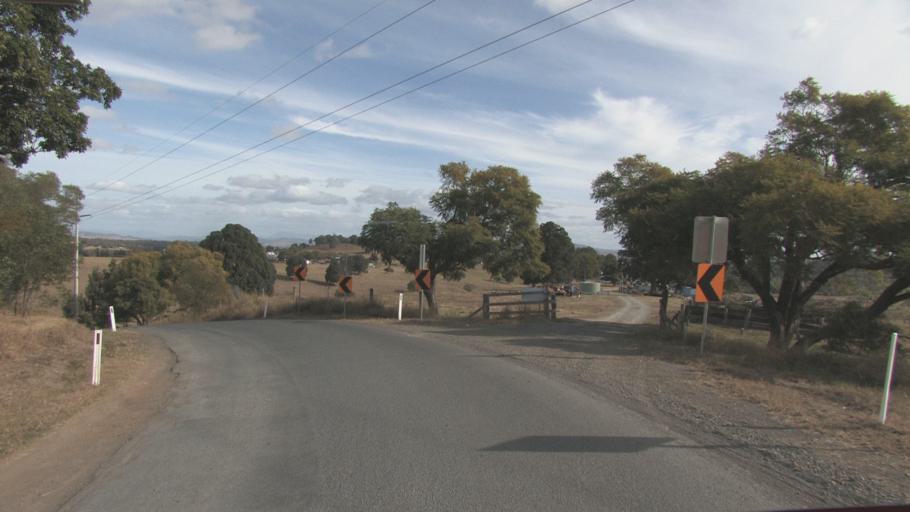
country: AU
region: Queensland
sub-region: Logan
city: Cedar Vale
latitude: -27.9009
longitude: 153.0154
